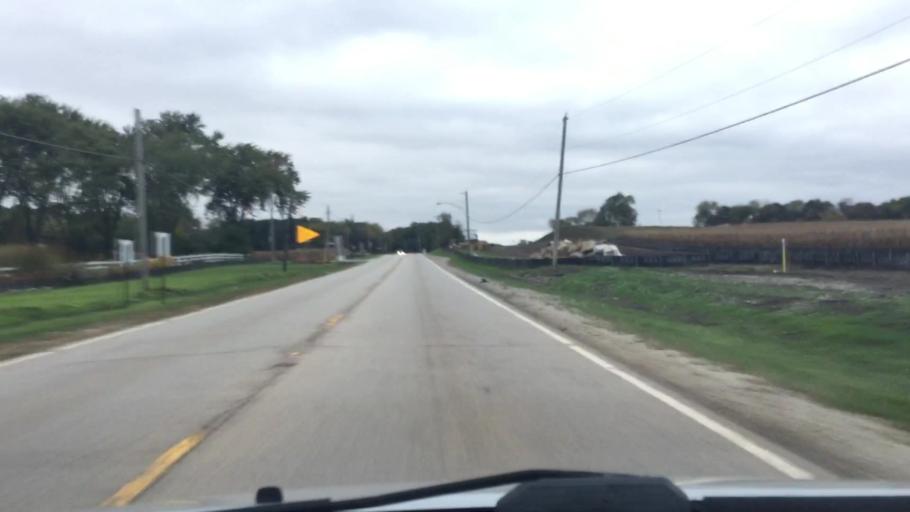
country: US
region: Illinois
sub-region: McHenry County
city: Algonquin
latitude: 42.1427
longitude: -88.2953
